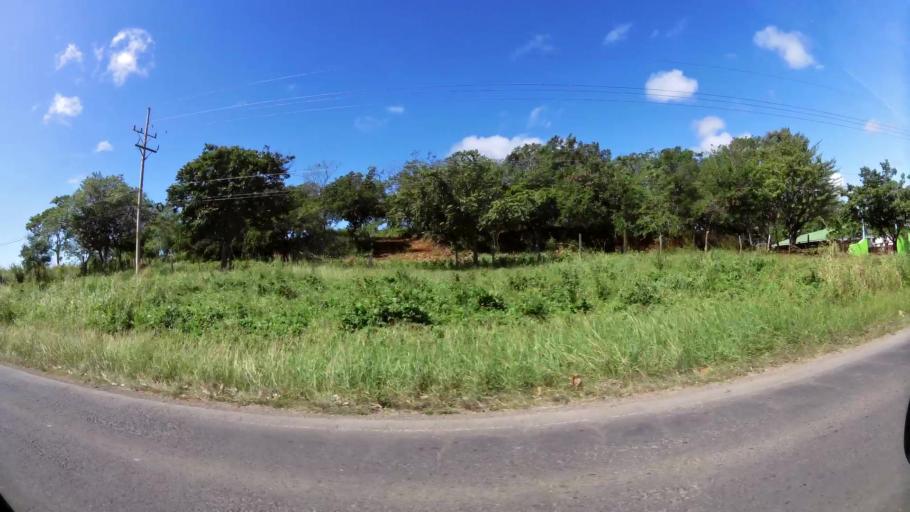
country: CR
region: Guanacaste
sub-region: Canton de Canas
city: Canas
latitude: 10.4099
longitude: -85.0852
